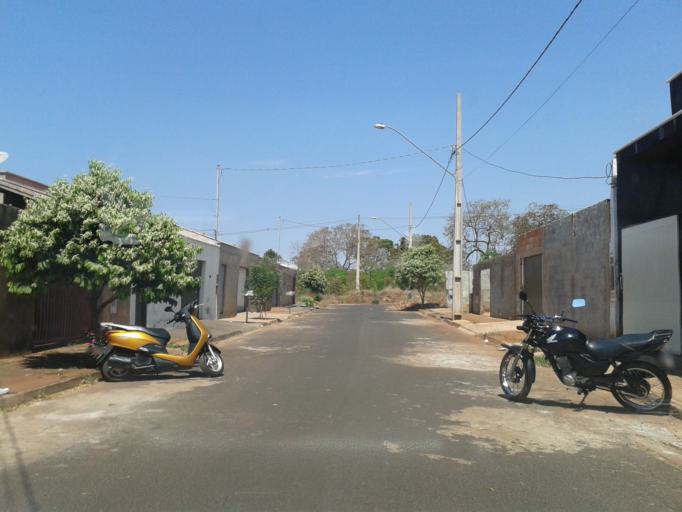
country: BR
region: Minas Gerais
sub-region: Ituiutaba
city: Ituiutaba
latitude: -18.9873
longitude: -49.4270
